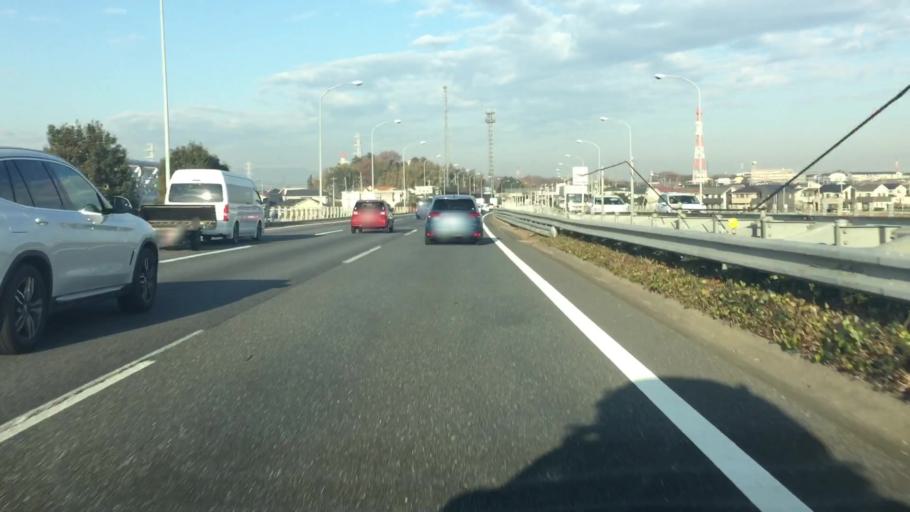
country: JP
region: Saitama
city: Sakado
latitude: 35.9176
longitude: 139.4200
